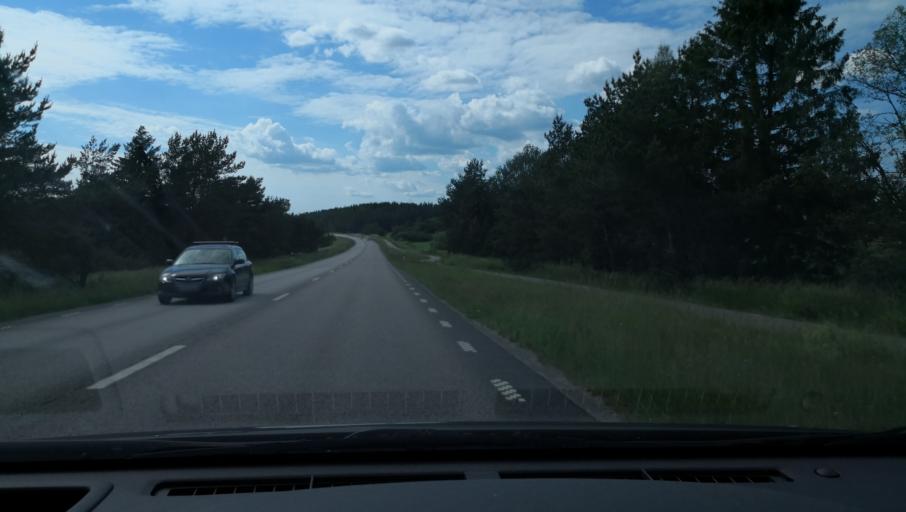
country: SE
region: Uppsala
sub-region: Uppsala Kommun
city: Uppsala
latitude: 59.8500
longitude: 17.5066
